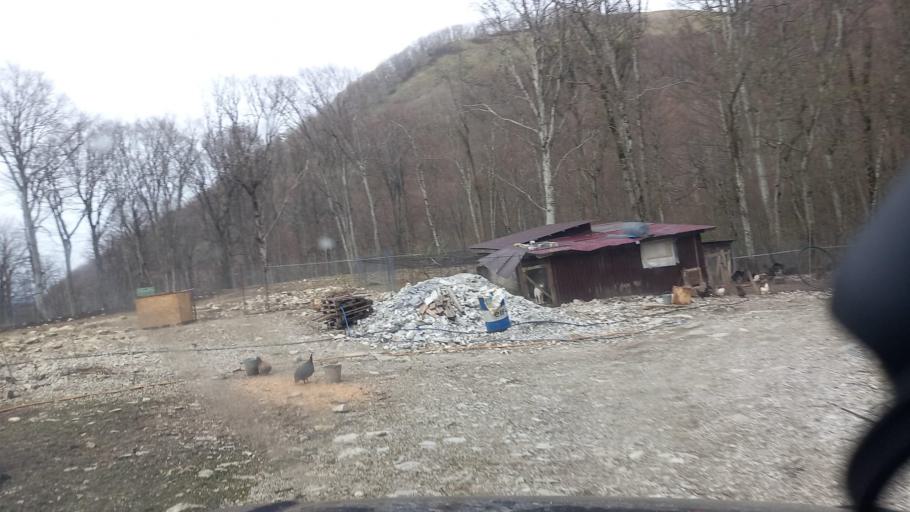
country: RU
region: Krasnodarskiy
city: Gelendzhik
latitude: 44.6165
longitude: 38.2046
